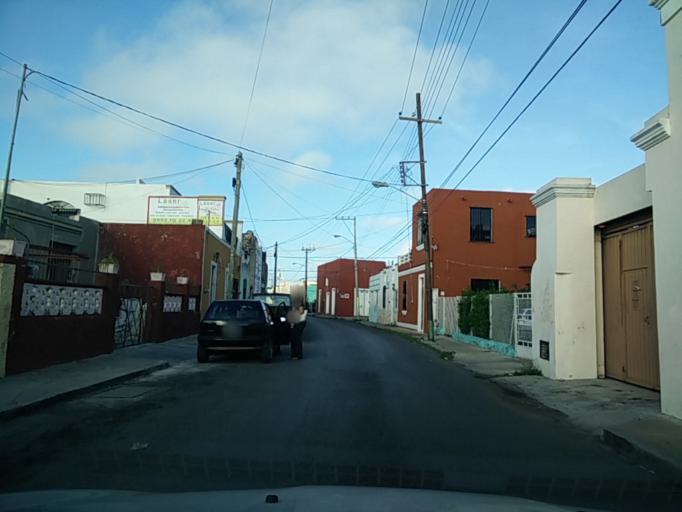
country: MX
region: Yucatan
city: Merida
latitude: 20.9675
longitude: -89.6353
